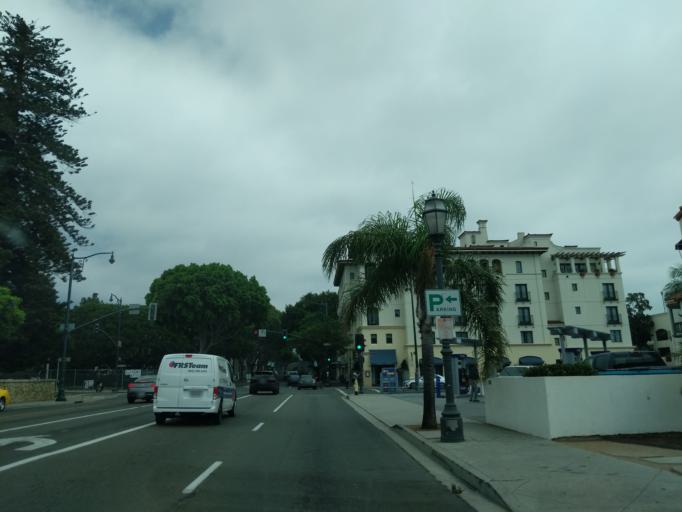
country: US
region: California
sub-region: Santa Barbara County
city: Santa Barbara
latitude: 34.4200
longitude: -119.7035
